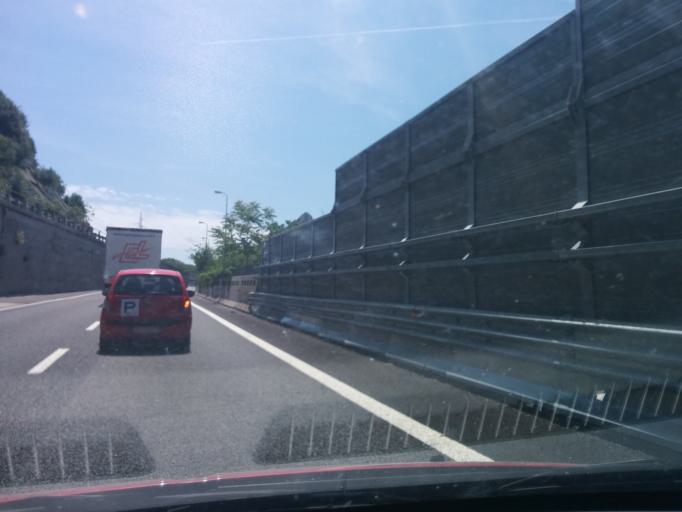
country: IT
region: Liguria
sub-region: Provincia di Genova
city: San Teodoro
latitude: 44.4262
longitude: 8.8952
